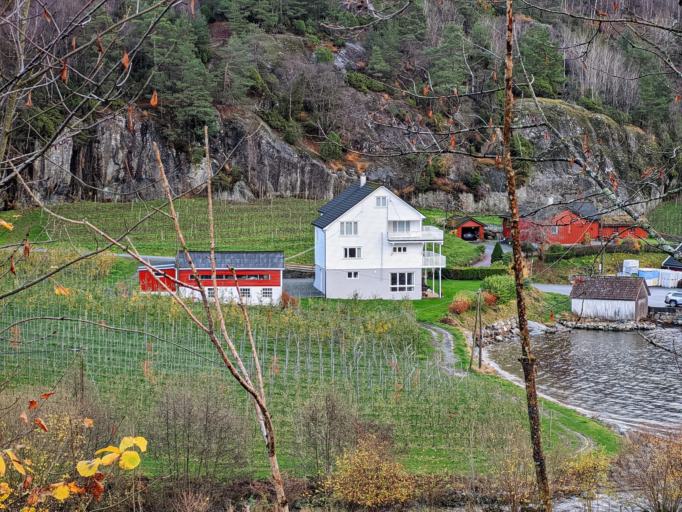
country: NO
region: Rogaland
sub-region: Hjelmeland
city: Hjelmelandsvagen
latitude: 59.2780
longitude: 6.1388
